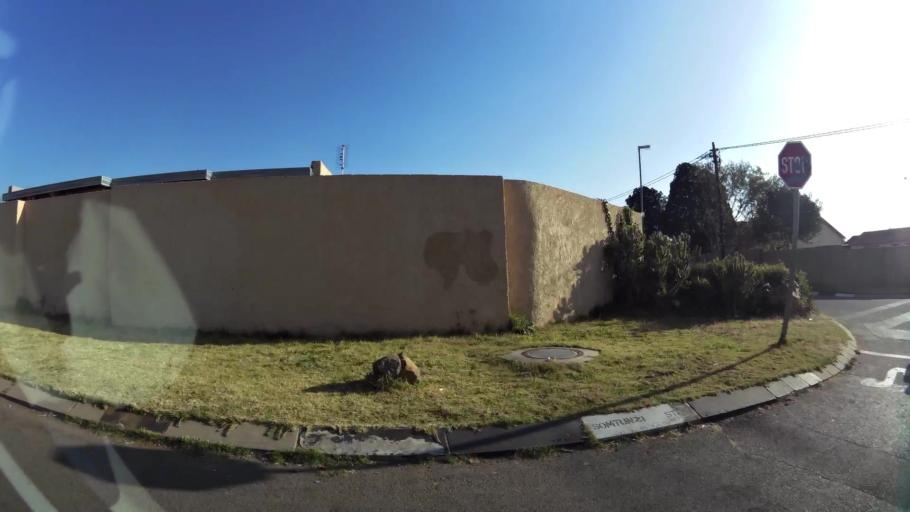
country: ZA
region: Gauteng
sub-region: City of Johannesburg Metropolitan Municipality
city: Soweto
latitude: -26.2635
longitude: 27.8738
